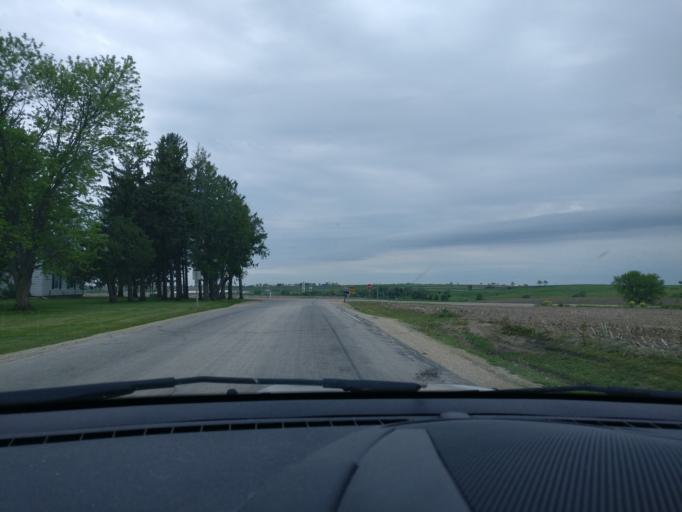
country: US
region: Wisconsin
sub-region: Lafayette County
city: Darlington
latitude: 42.7534
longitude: -90.0115
